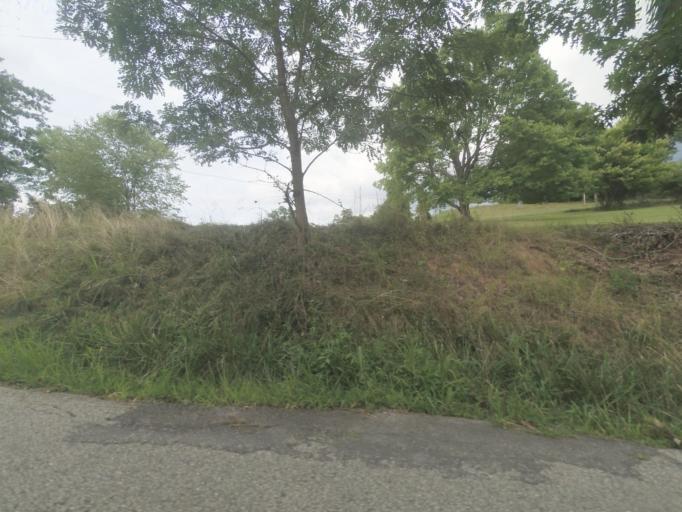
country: US
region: West Virginia
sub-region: Cabell County
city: Huntington
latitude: 38.3849
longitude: -82.4137
